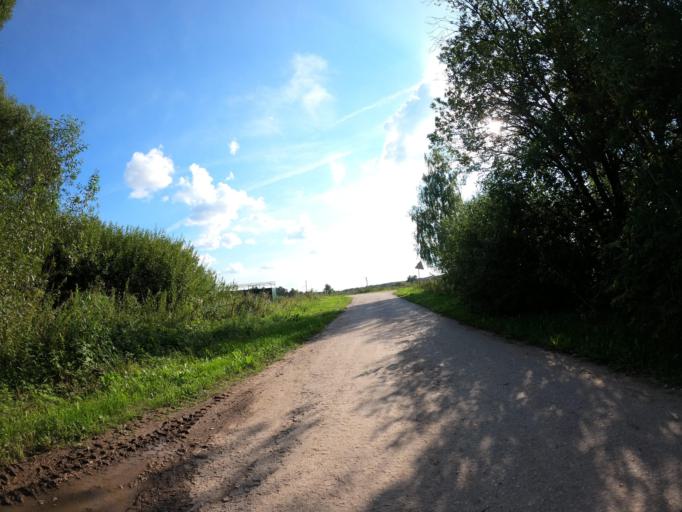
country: RU
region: Moskovskaya
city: Troitskoye
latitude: 55.2120
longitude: 38.4852
